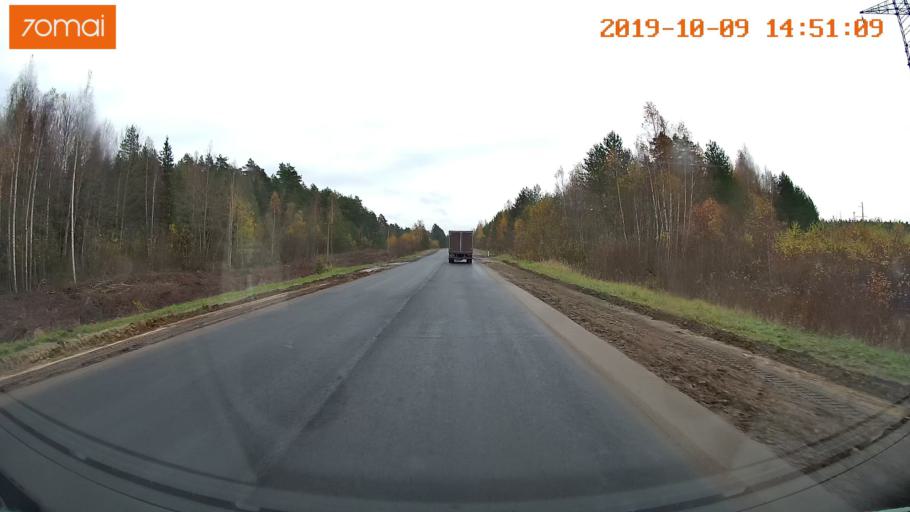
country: RU
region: Kostroma
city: Chistyye Bory
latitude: 58.3792
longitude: 41.6113
